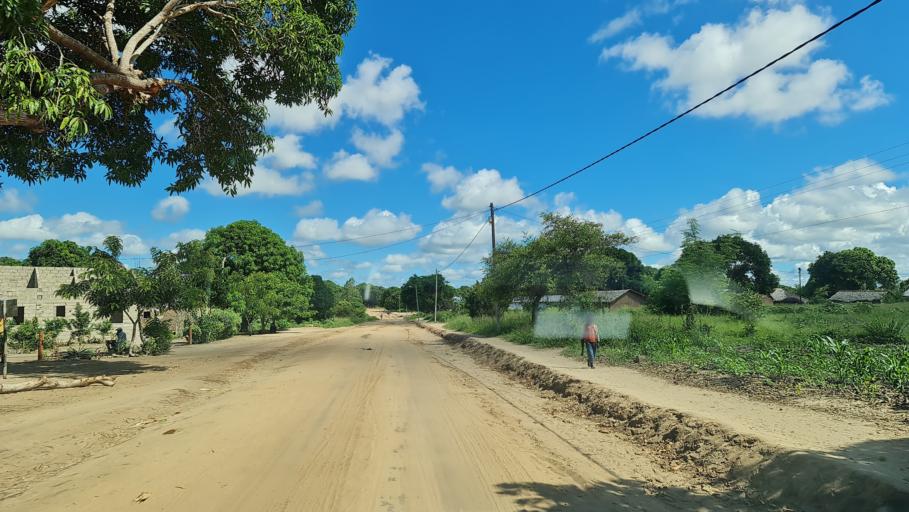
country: MZ
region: Nampula
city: Ilha de Mocambique
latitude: -15.5521
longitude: 40.4077
